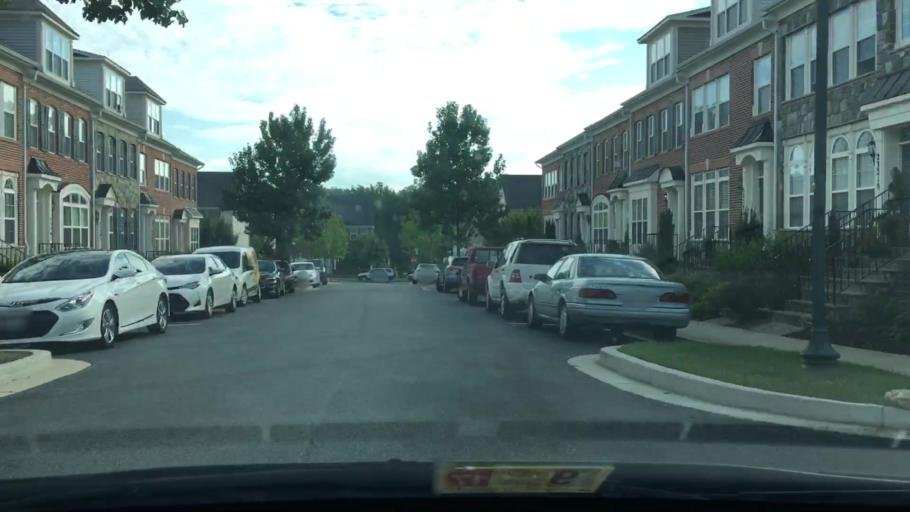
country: US
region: Maryland
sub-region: Montgomery County
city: Clarksburg
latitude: 39.2379
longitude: -77.2633
